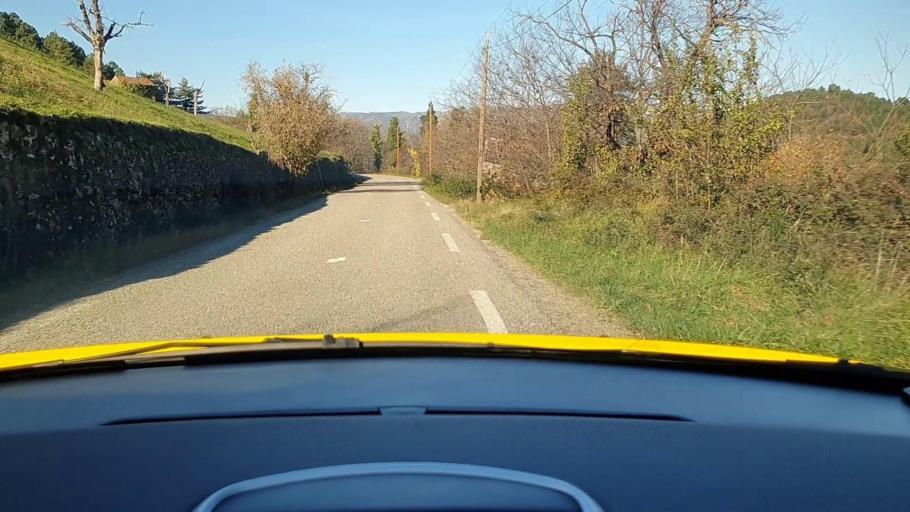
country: FR
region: Languedoc-Roussillon
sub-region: Departement du Gard
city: Branoux-les-Taillades
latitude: 44.2820
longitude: 3.9927
